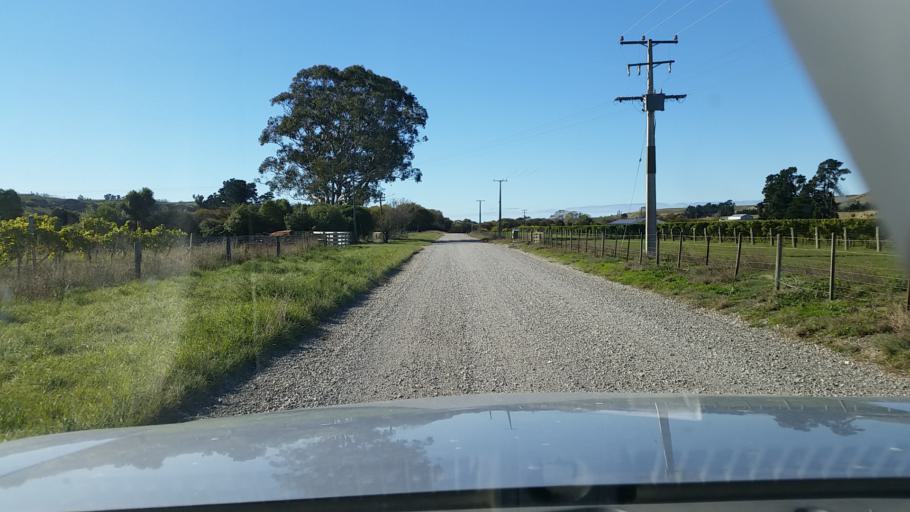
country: NZ
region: Marlborough
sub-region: Marlborough District
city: Blenheim
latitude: -41.6815
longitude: 174.1330
